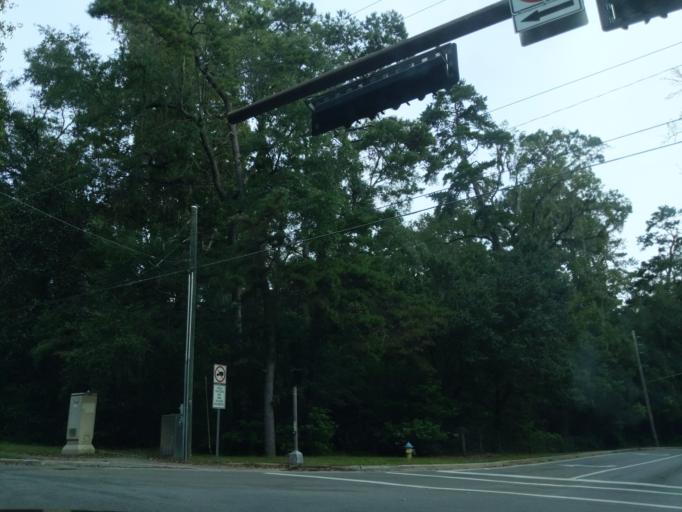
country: US
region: Florida
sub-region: Leon County
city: Tallahassee
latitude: 30.4631
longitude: -84.2599
